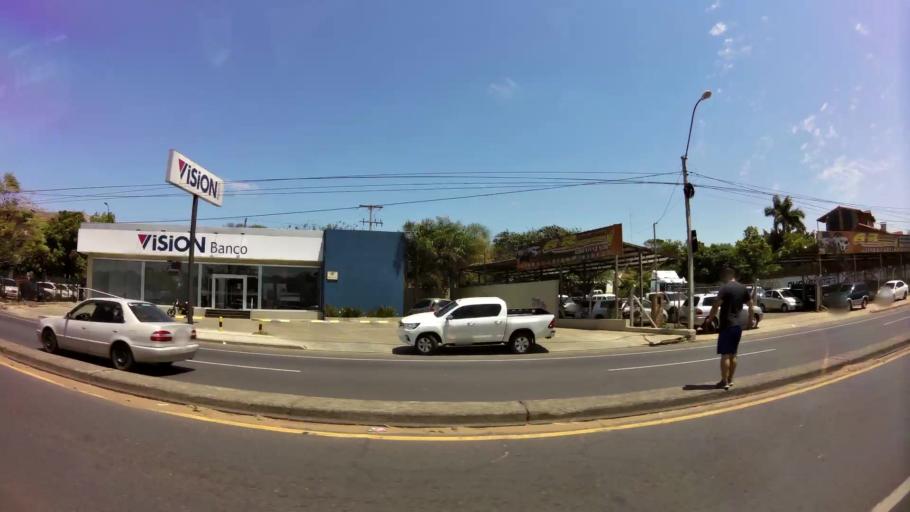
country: PY
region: Central
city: Nemby
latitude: -25.3918
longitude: -57.5454
